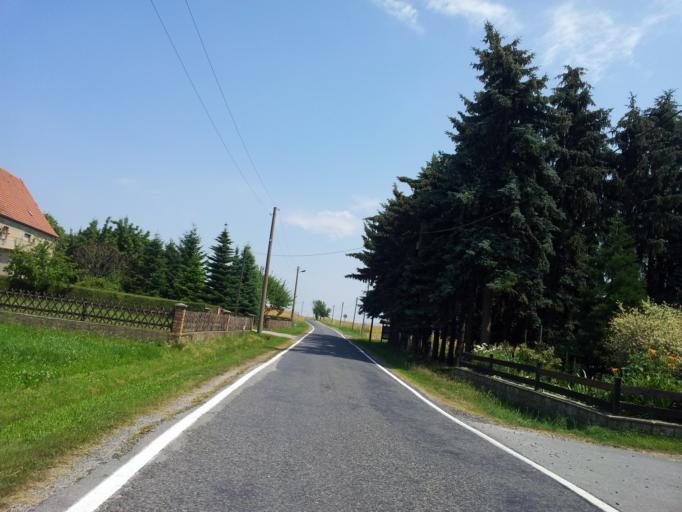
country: DE
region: Saxony
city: Panschwitz-Kuckau
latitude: 51.2060
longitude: 14.2099
